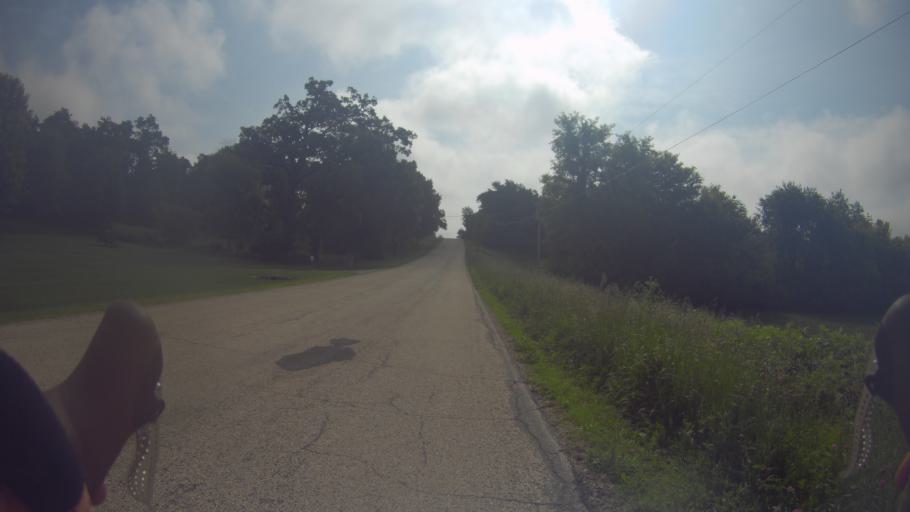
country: US
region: Wisconsin
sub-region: Dane County
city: Stoughton
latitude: 42.9410
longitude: -89.1769
